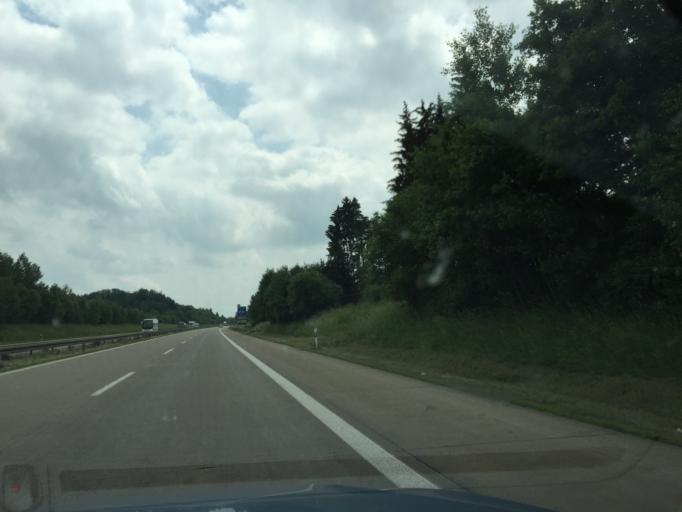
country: DE
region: Baden-Wuerttemberg
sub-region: Regierungsbezirk Stuttgart
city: Ellenberg
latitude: 48.9945
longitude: 10.1944
